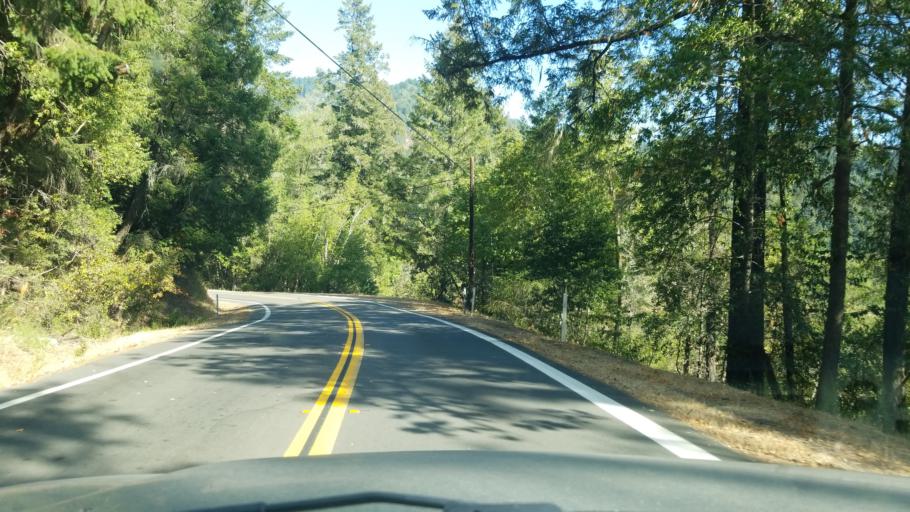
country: US
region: California
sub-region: Humboldt County
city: Redway
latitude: 40.2220
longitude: -123.7935
